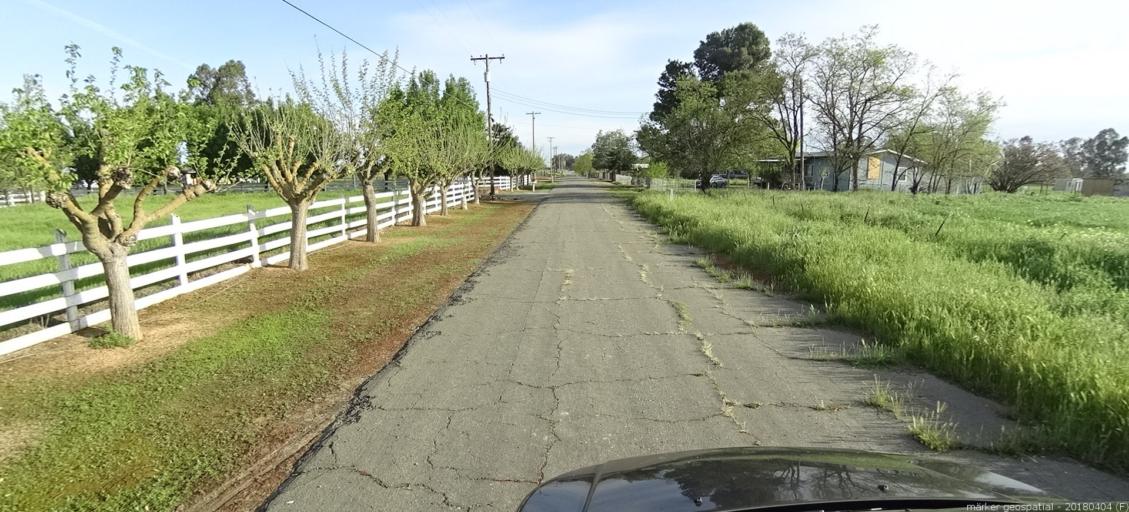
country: US
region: California
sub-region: Sacramento County
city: Herald
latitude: 38.3370
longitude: -121.2467
